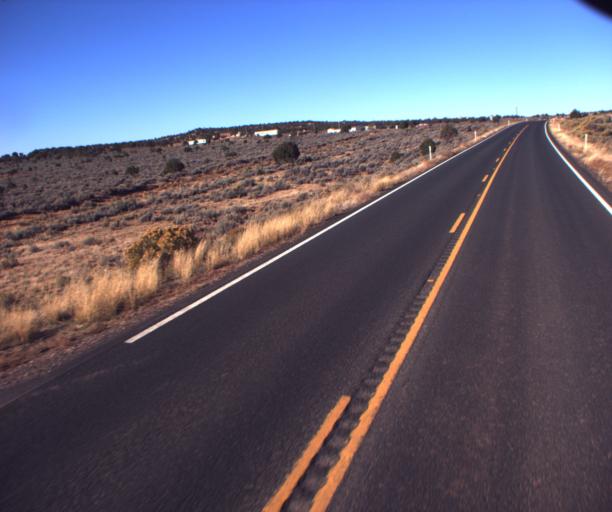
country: US
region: Arizona
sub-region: Apache County
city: Ganado
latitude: 35.7604
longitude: -109.7708
